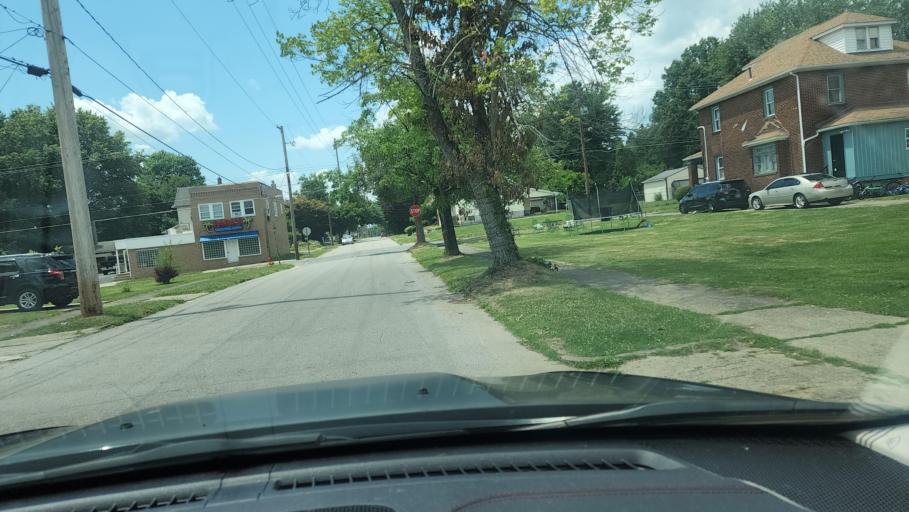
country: US
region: Ohio
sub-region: Mahoning County
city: Campbell
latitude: 41.0786
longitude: -80.5930
